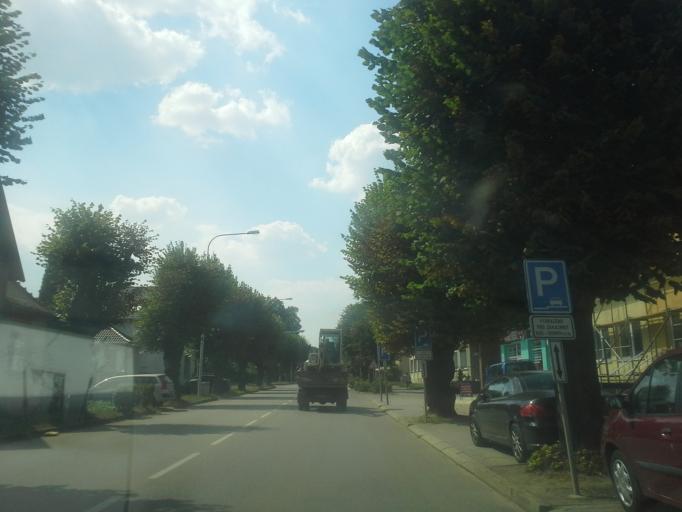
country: CZ
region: South Moravian
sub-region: Okres Blansko
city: Boskovice
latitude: 49.4921
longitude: 16.6547
